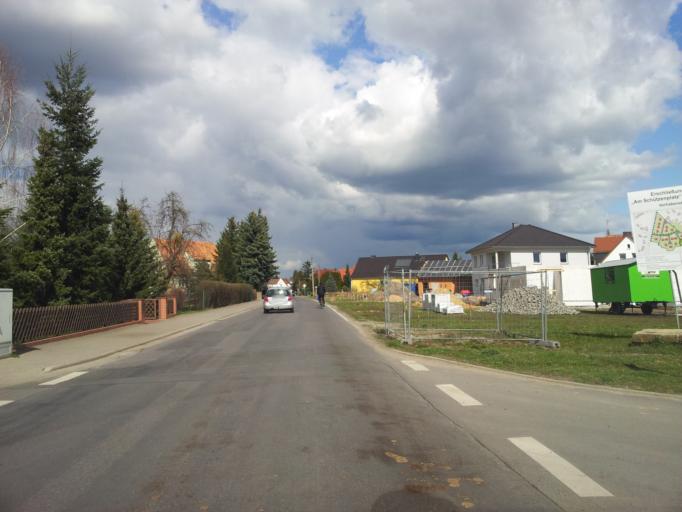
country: DE
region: Saxony
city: Wittichenau
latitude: 51.3798
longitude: 14.2434
